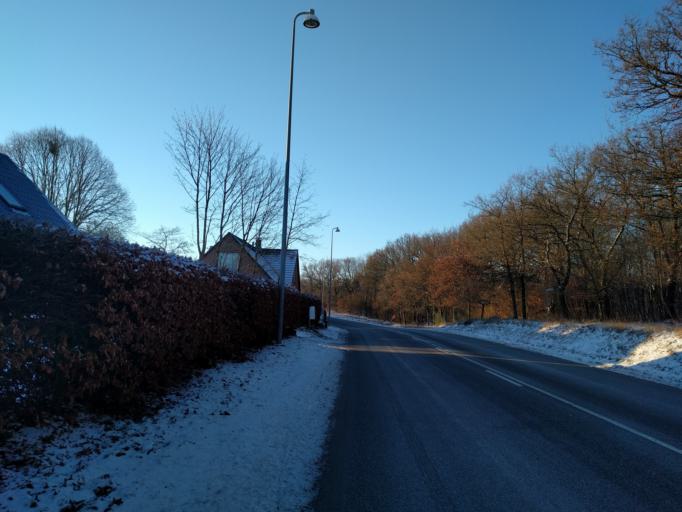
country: DK
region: Central Jutland
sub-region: Viborg Kommune
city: Viborg
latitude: 56.4254
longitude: 9.3828
